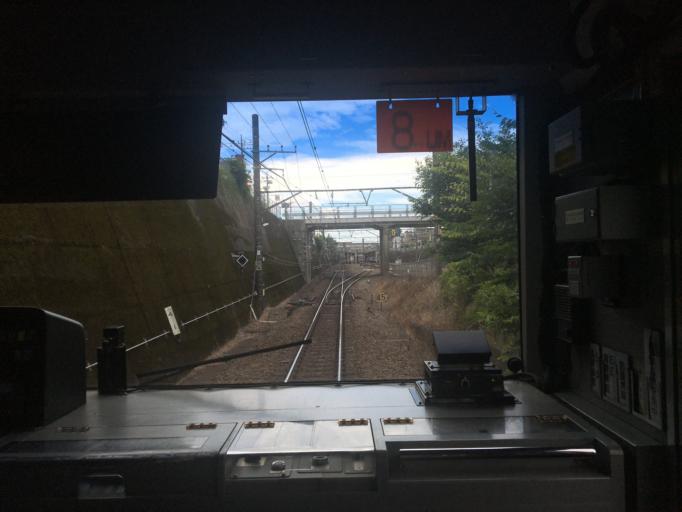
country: JP
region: Saitama
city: Tokorozawa
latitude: 35.7968
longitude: 139.5190
